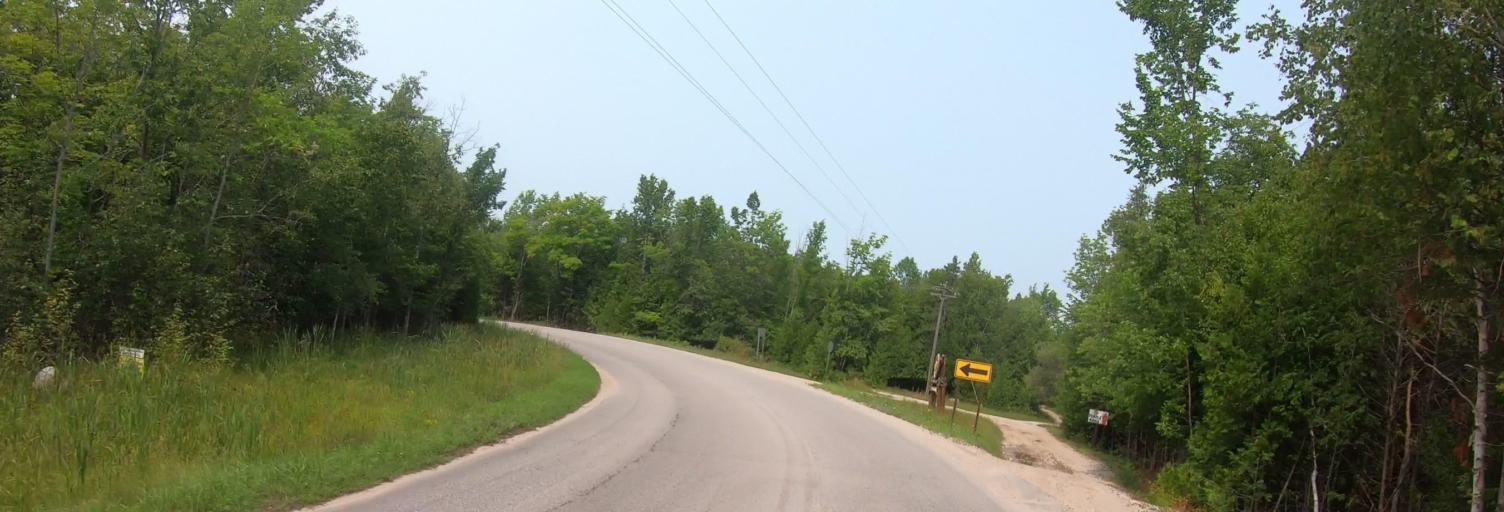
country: CA
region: Ontario
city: Thessalon
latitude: 46.0198
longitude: -83.7183
